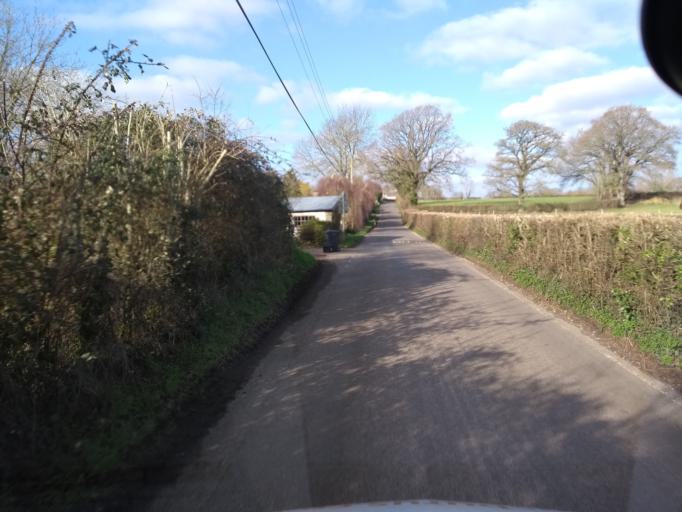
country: GB
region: England
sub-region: Somerset
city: Chard
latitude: 50.9311
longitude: -2.9728
